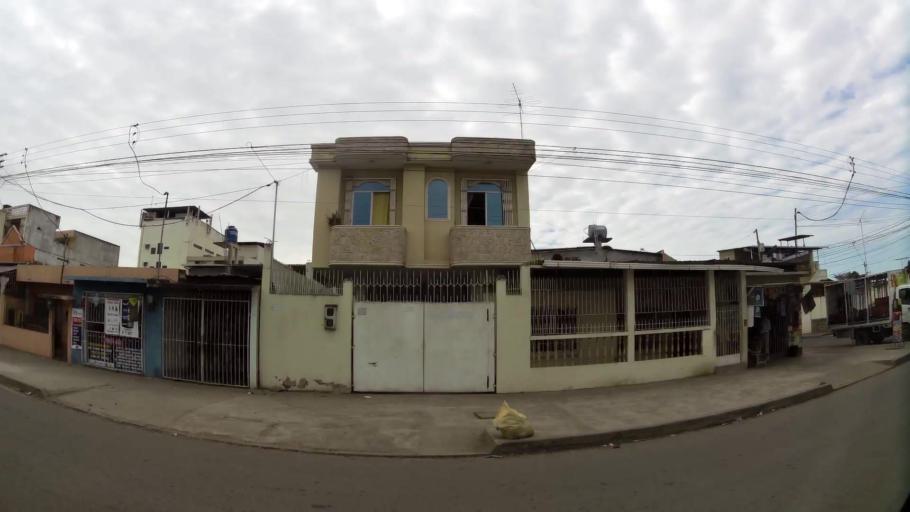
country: EC
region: El Oro
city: Machala
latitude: -3.2495
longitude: -79.9500
